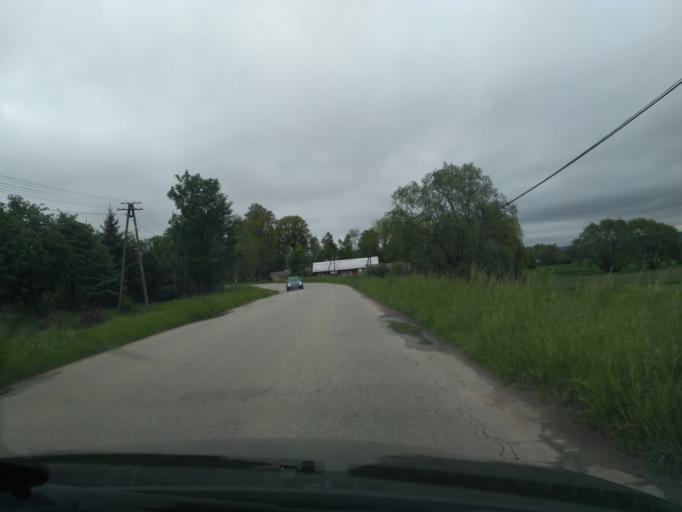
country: PL
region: Subcarpathian Voivodeship
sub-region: Powiat jasielski
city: Brzyska
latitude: 49.8351
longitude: 21.3930
